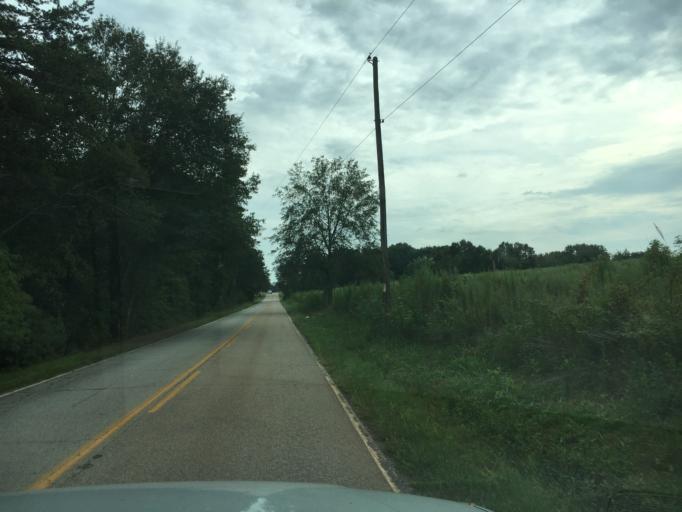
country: US
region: South Carolina
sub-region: Spartanburg County
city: Duncan
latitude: 34.9271
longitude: -82.1644
